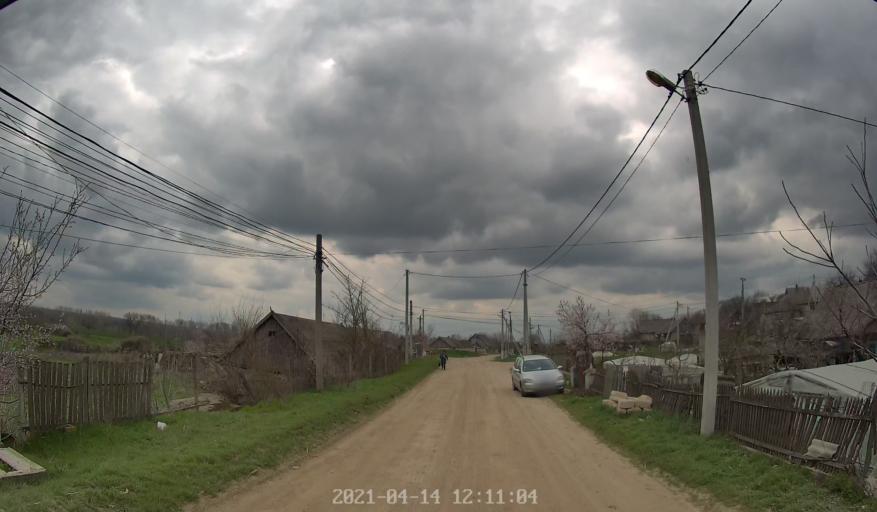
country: MD
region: Criuleni
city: Criuleni
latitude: 47.1671
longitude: 29.2044
